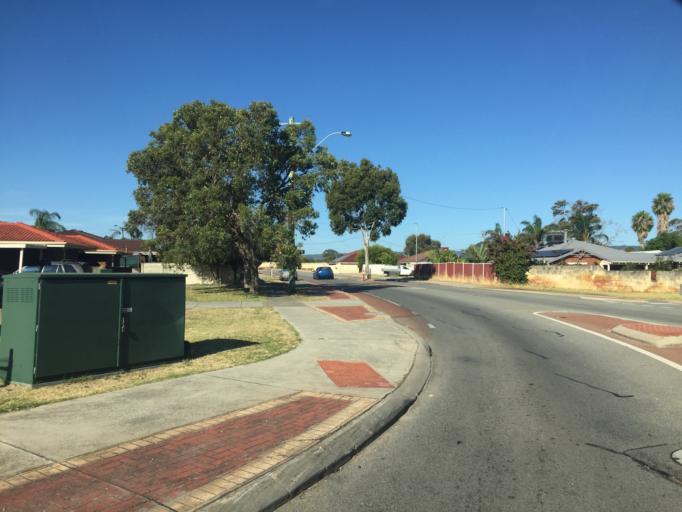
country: AU
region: Western Australia
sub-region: Canning
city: East Cannington
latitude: -32.0090
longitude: 115.9706
